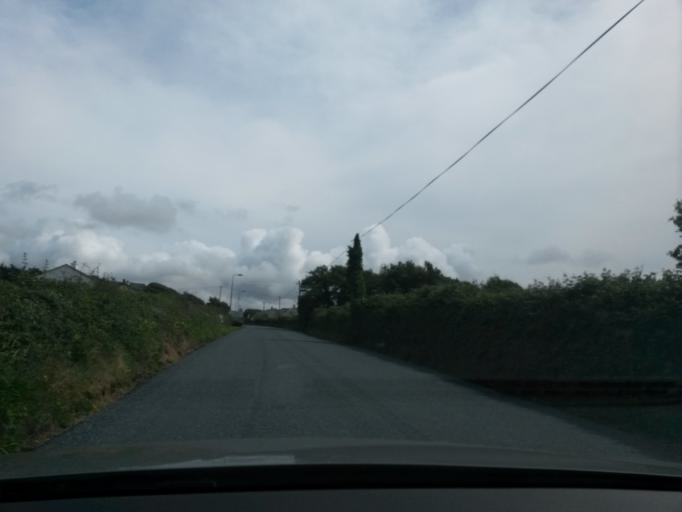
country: IE
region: Connaught
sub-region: Sligo
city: Sligo
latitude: 54.4330
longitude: -8.4571
